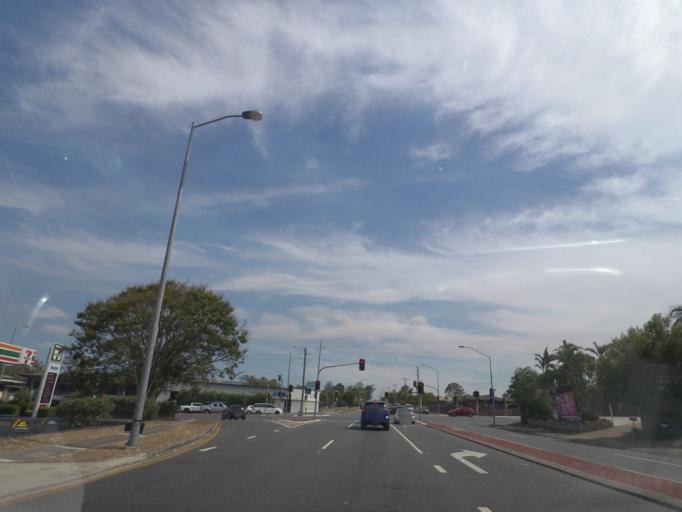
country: AU
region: Queensland
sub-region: Brisbane
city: Sunnybank Hills
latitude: -27.6109
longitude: 153.0622
